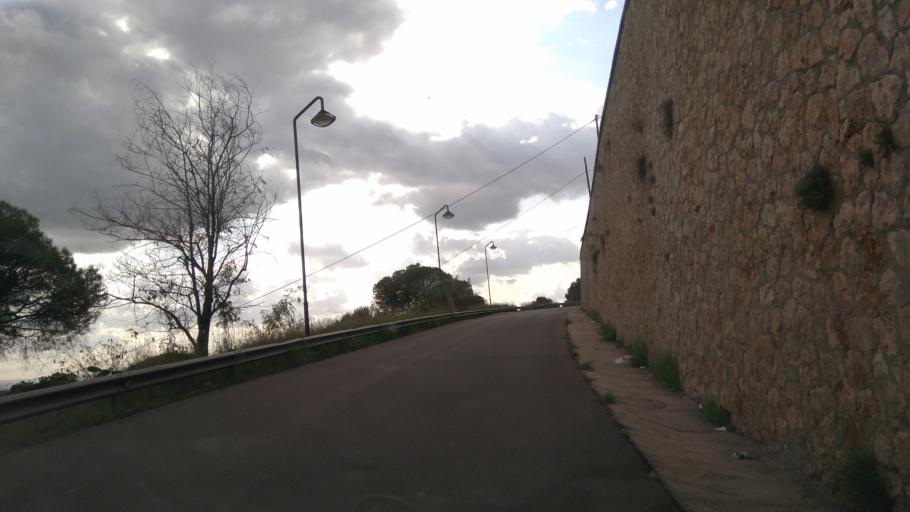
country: ES
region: Valencia
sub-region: Provincia de Valencia
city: Alzira
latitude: 39.1525
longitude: -0.4177
